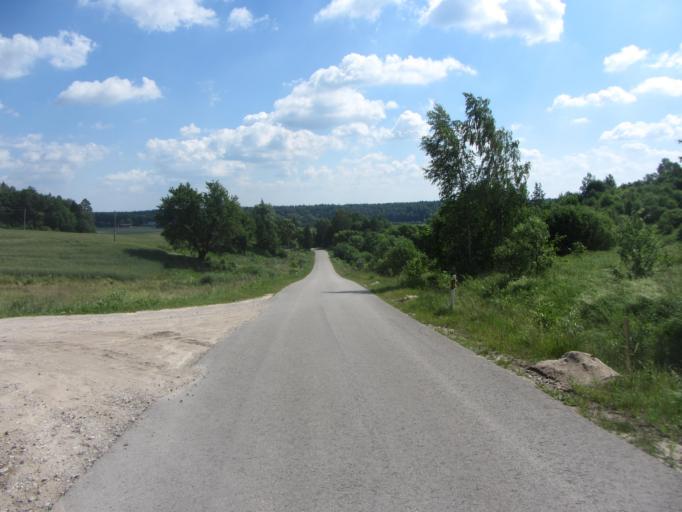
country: LT
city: Birstonas
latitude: 54.5240
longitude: 23.9809
